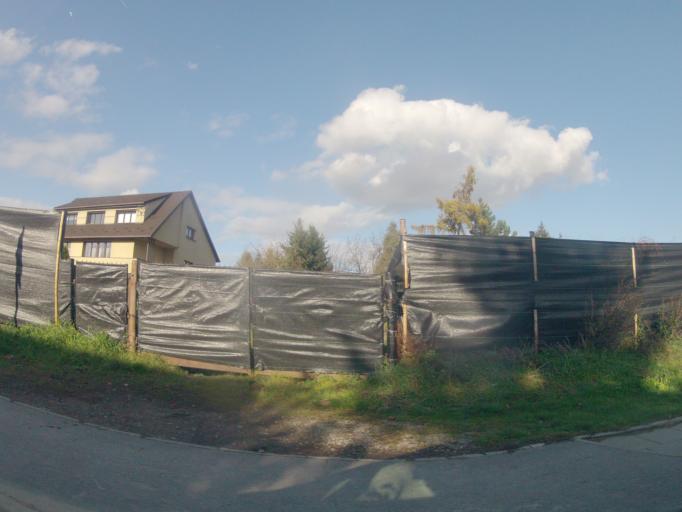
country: PL
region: Lesser Poland Voivodeship
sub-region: Powiat krakowski
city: Rzaska
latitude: 50.0676
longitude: 19.8495
